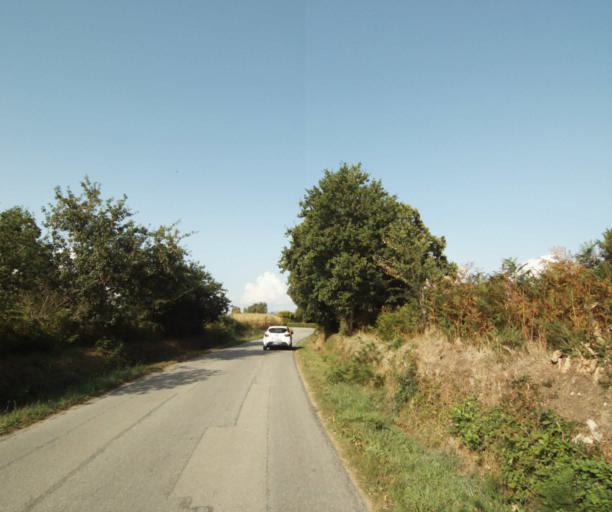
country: FR
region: Brittany
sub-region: Departement du Morbihan
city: Riantec
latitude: 47.7299
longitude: -3.2969
